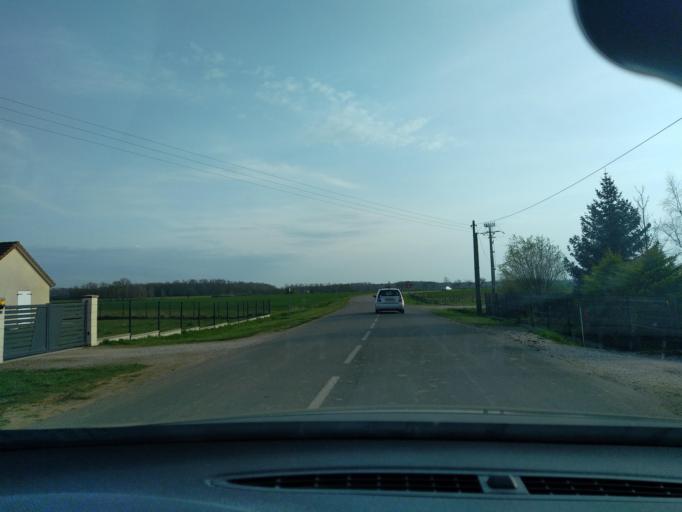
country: FR
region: Franche-Comte
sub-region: Departement du Jura
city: Chaussin
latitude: 46.9752
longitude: 5.4264
